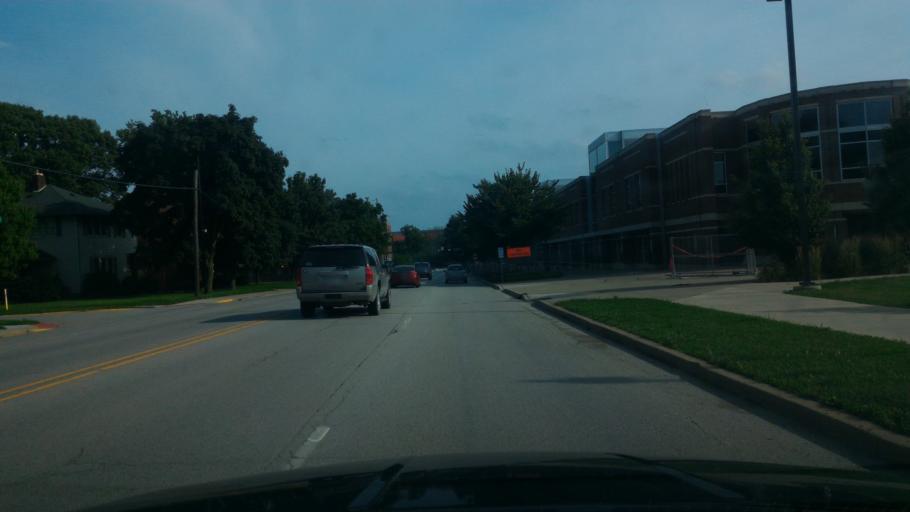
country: US
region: Indiana
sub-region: Tippecanoe County
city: West Lafayette
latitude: 40.4351
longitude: -86.9154
